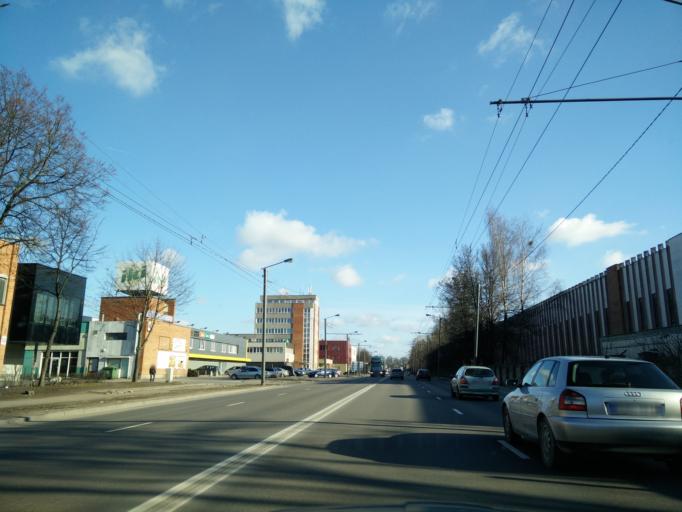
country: LT
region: Kauno apskritis
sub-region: Kauno rajonas
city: Akademija (Kaunas)
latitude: 54.9146
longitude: 23.8394
